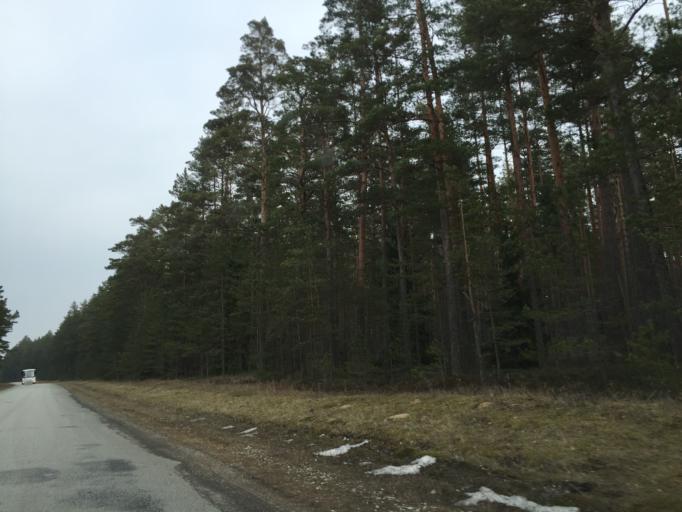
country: LV
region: Salacgrivas
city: Ainazi
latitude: 57.9777
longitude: 24.4142
